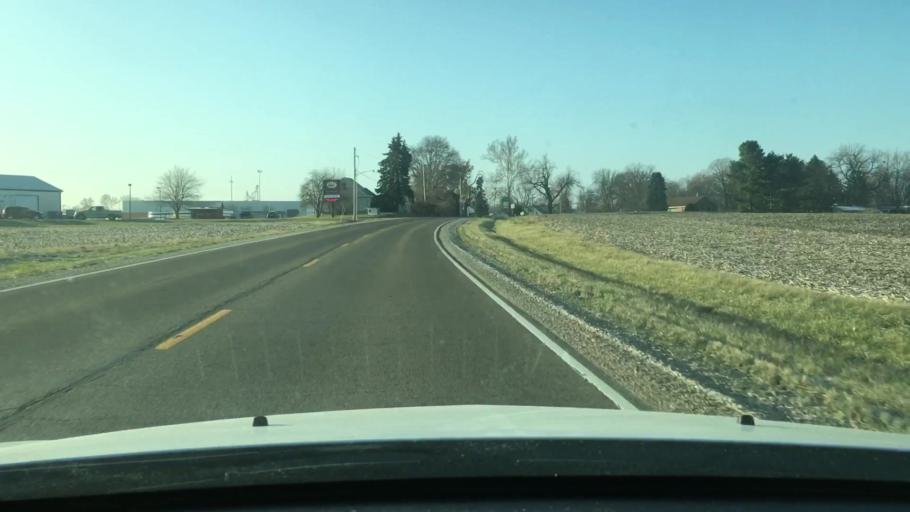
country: US
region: Illinois
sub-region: Woodford County
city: Metamora
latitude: 40.8004
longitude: -89.3568
